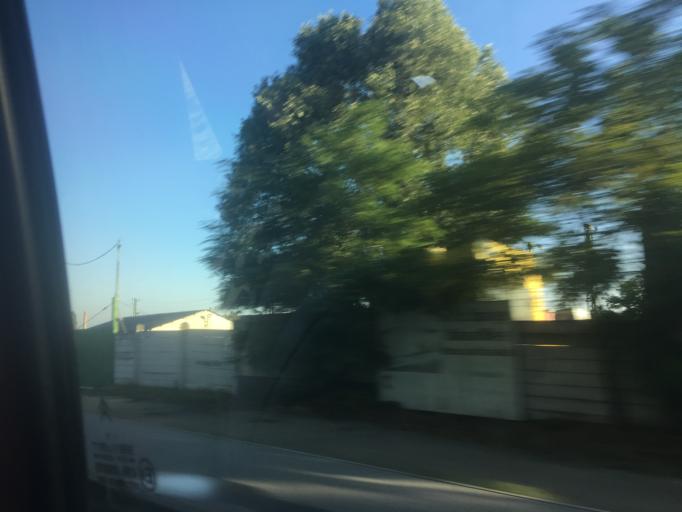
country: HU
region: Budapest
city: Budapest X. keruelet
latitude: 47.4889
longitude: 19.1695
